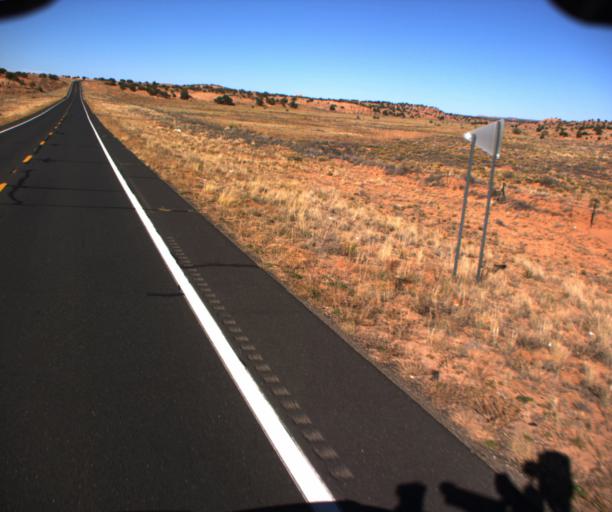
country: US
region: Arizona
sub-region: Coconino County
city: Kaibito
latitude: 36.4963
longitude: -110.7056
